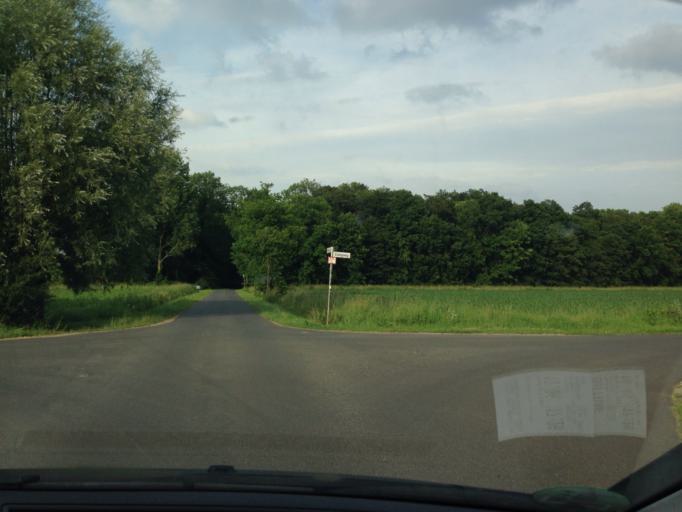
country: DE
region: North Rhine-Westphalia
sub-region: Regierungsbezirk Munster
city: Altenberge
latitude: 52.0116
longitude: 7.5361
